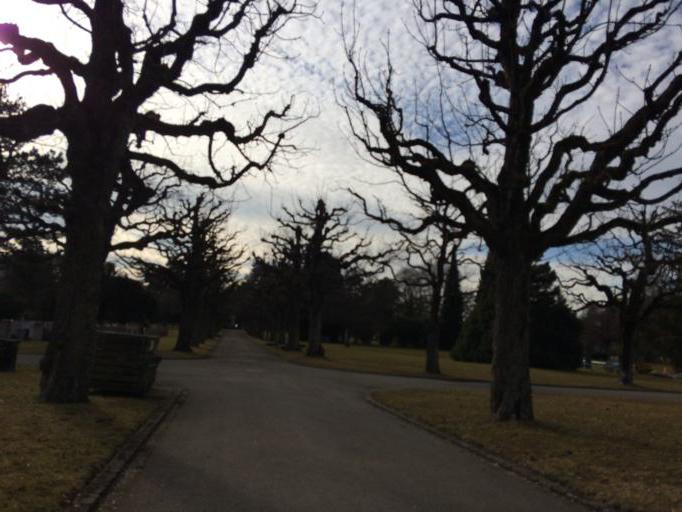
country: CH
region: Bern
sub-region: Bern-Mittelland District
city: Koniz
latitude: 46.9497
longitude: 7.4200
